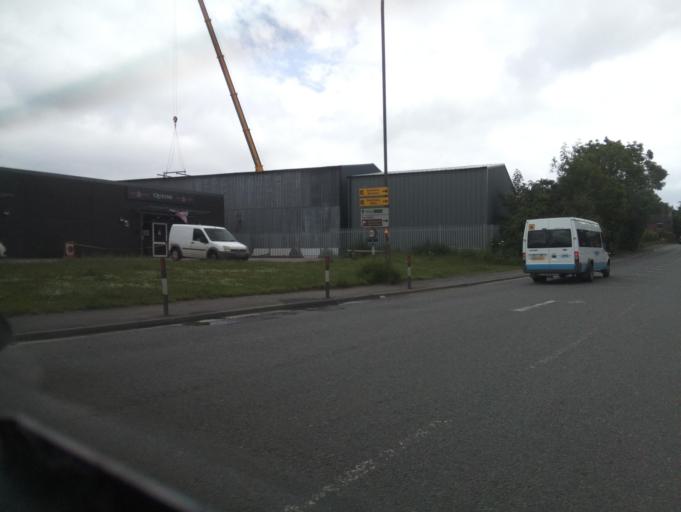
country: GB
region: England
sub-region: Derbyshire
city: Ashbourne
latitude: 53.0069
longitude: -1.7187
